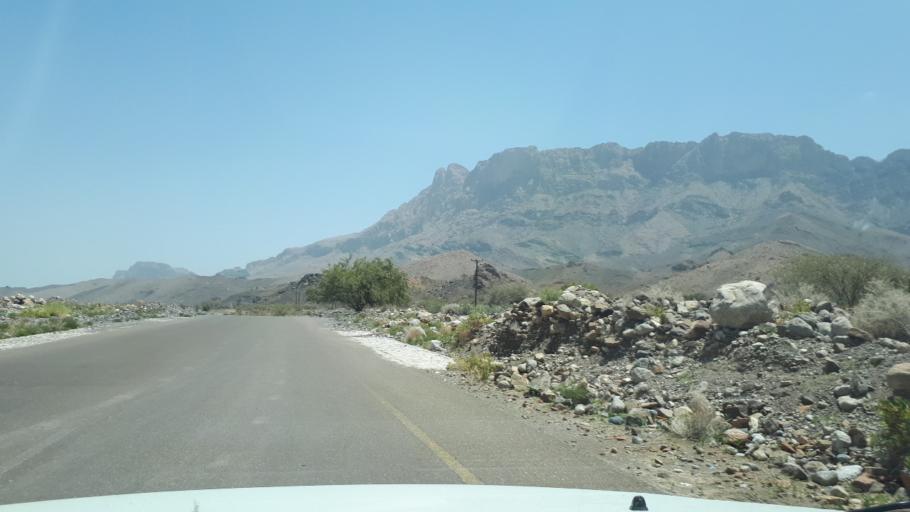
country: OM
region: Muhafazat ad Dakhiliyah
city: Bahla'
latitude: 23.1657
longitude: 57.1602
